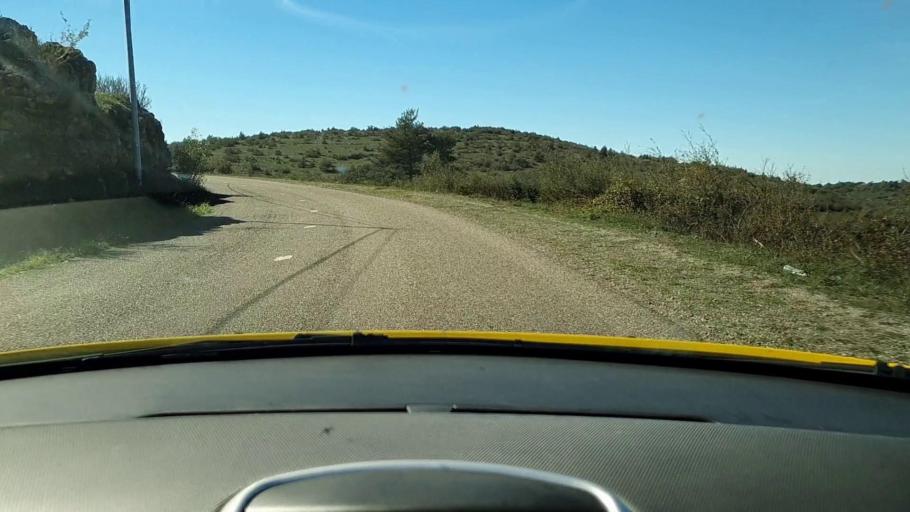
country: FR
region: Languedoc-Roussillon
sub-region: Departement du Gard
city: Aveze
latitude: 43.9612
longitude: 3.4081
